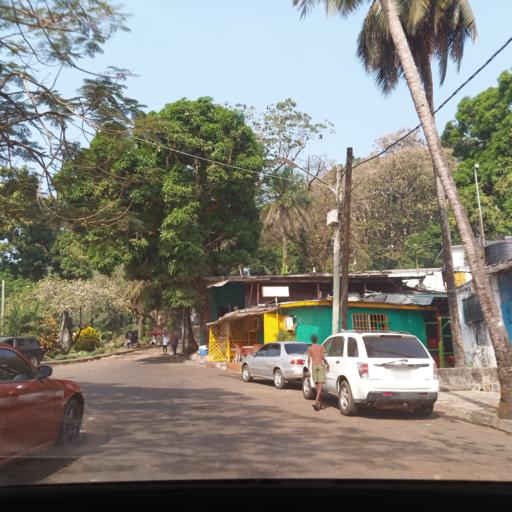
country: LR
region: Montserrado
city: Monrovia
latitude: 6.3192
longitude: -10.8119
